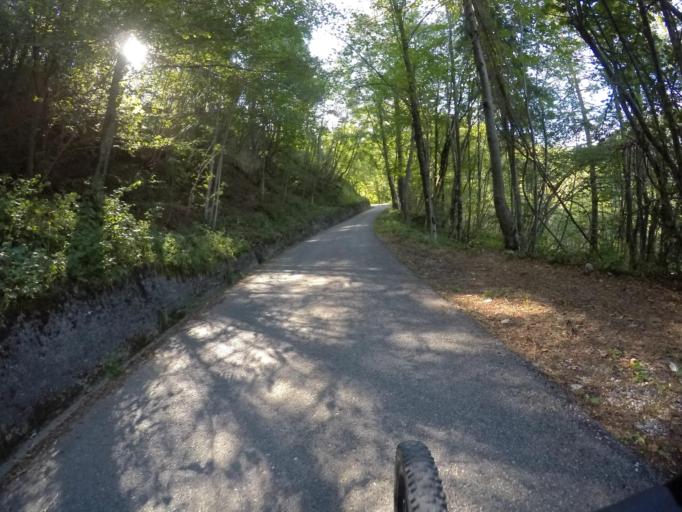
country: IT
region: Friuli Venezia Giulia
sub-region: Provincia di Udine
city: Zuglio
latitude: 46.4400
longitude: 13.0853
